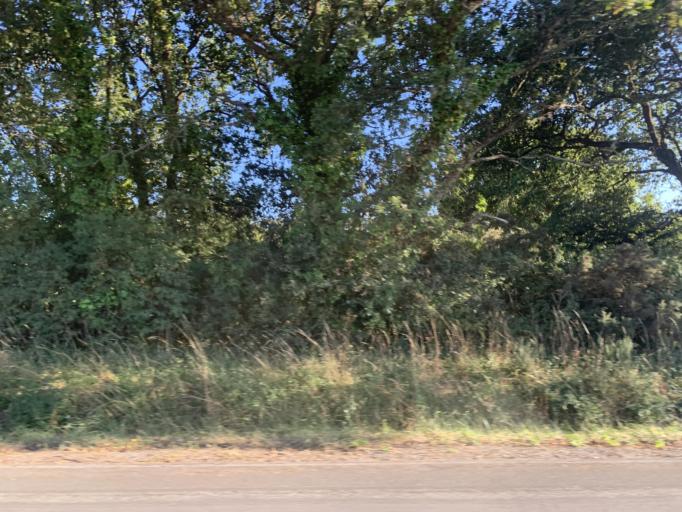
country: FR
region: Pays de la Loire
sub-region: Departement de la Loire-Atlantique
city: Pornichet
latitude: 47.2595
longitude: -2.2899
